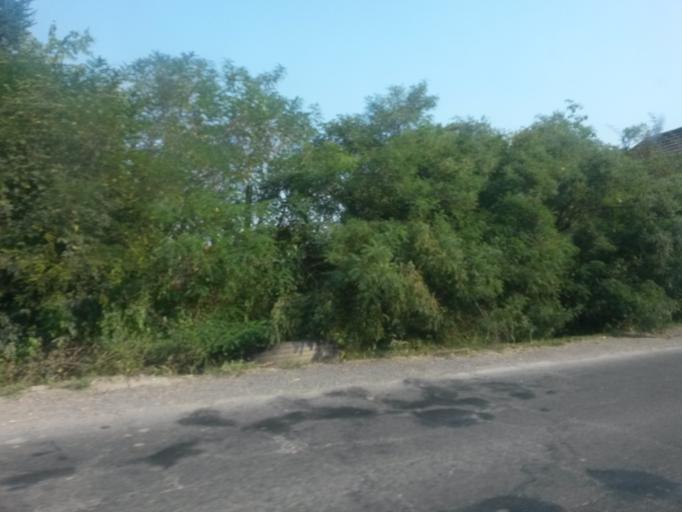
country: RO
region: Cluj
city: Turda
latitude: 46.5613
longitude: 23.7748
